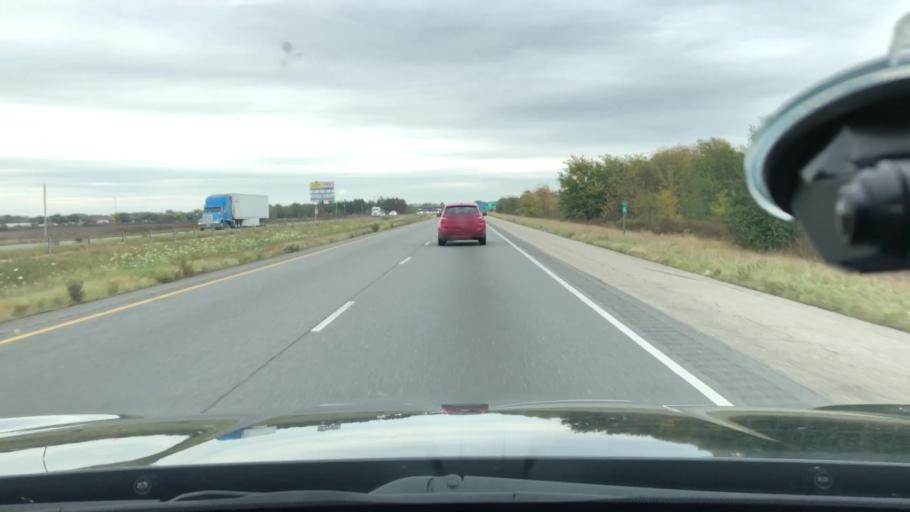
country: US
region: Arkansas
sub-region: Miller County
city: Texarkana
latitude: 33.5049
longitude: -93.9524
